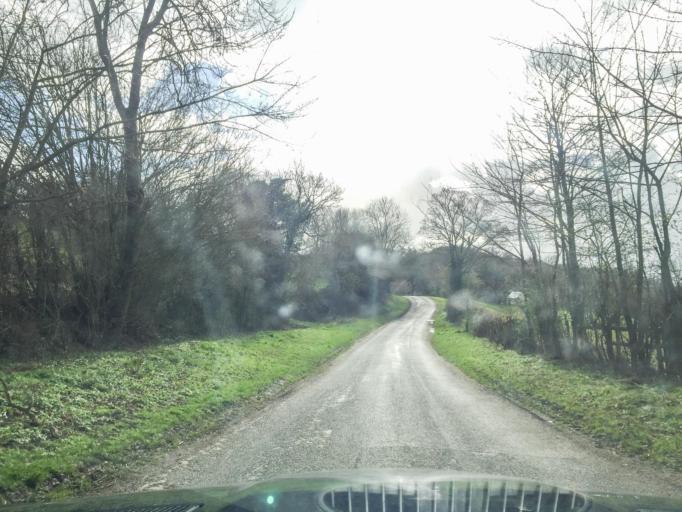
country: GB
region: England
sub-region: Warwickshire
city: Shipston on Stour
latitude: 52.0618
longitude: -1.5548
